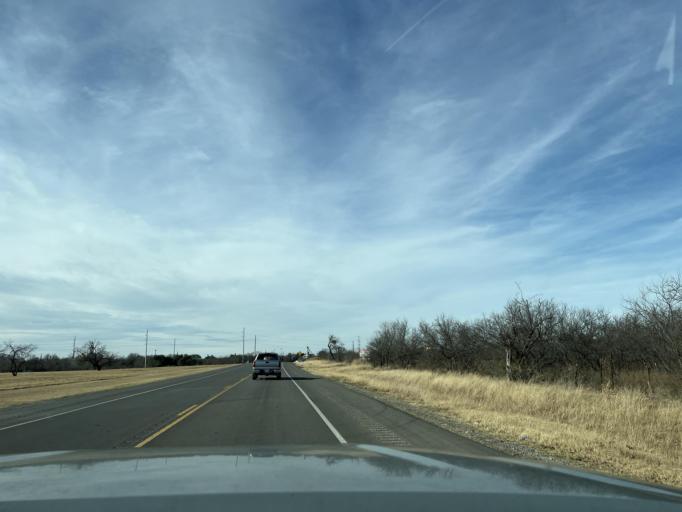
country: US
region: Texas
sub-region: Shackelford County
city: Albany
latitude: 32.7202
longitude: -99.2897
